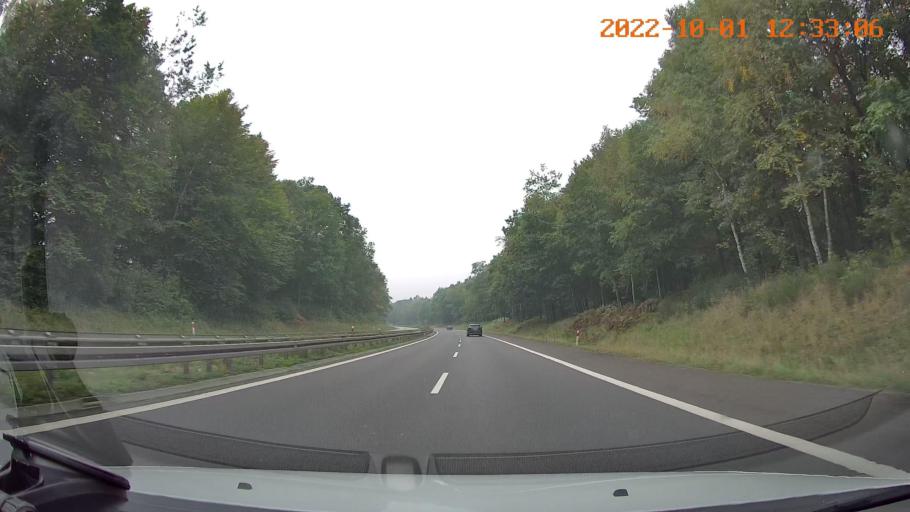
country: PL
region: Silesian Voivodeship
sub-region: Powiat bierunsko-ledzinski
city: Ledziny
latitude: 50.1540
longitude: 19.1209
